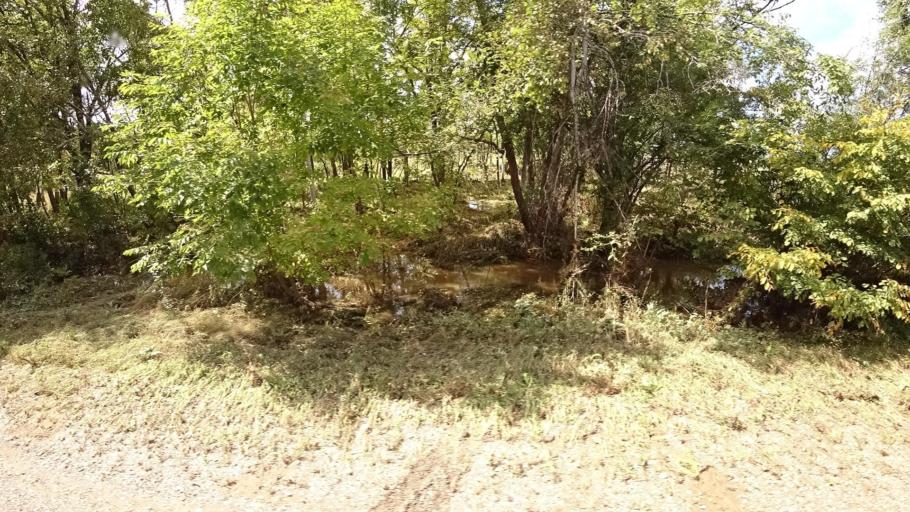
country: RU
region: Primorskiy
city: Yakovlevka
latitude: 44.6650
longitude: 133.7507
